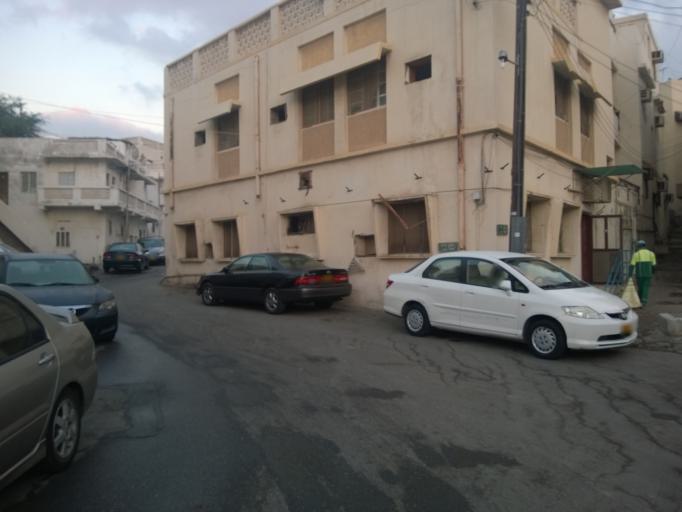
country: OM
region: Muhafazat Masqat
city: Muscat
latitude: 23.6210
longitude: 58.5611
